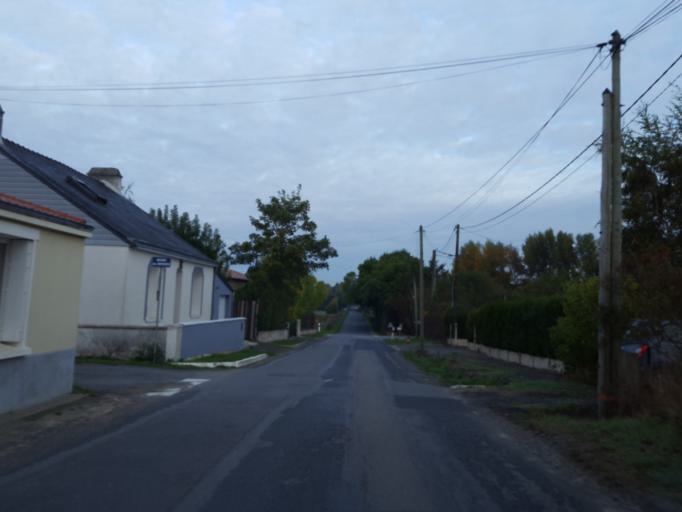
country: FR
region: Pays de la Loire
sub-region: Departement de la Loire-Atlantique
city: Saint-Julien-de-Concelles
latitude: 47.2493
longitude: -1.4036
